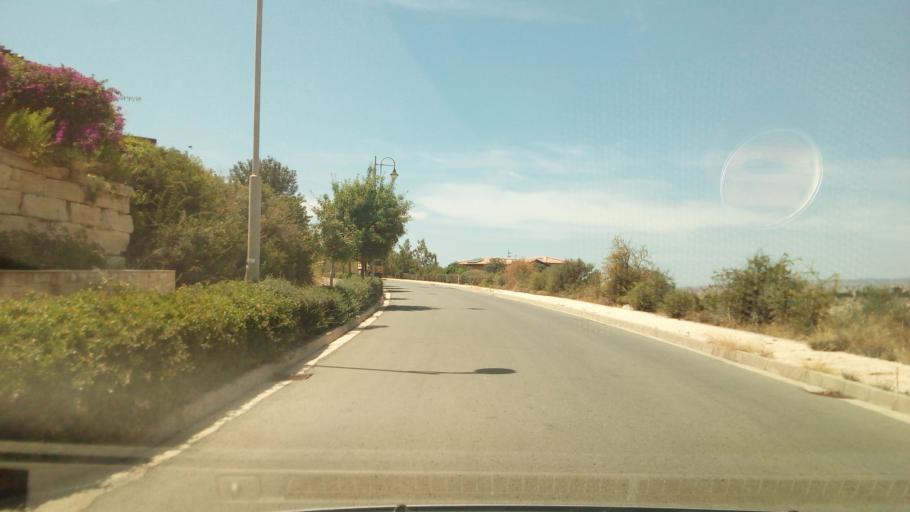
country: CY
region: Limassol
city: Pissouri
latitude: 34.6875
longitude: 32.6050
